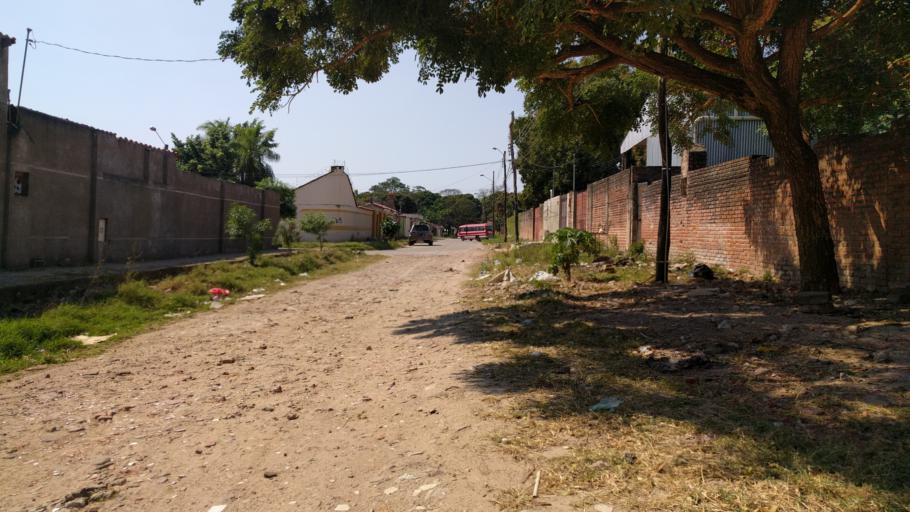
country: BO
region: Santa Cruz
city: Santa Cruz de la Sierra
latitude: -17.7982
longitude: -63.2244
